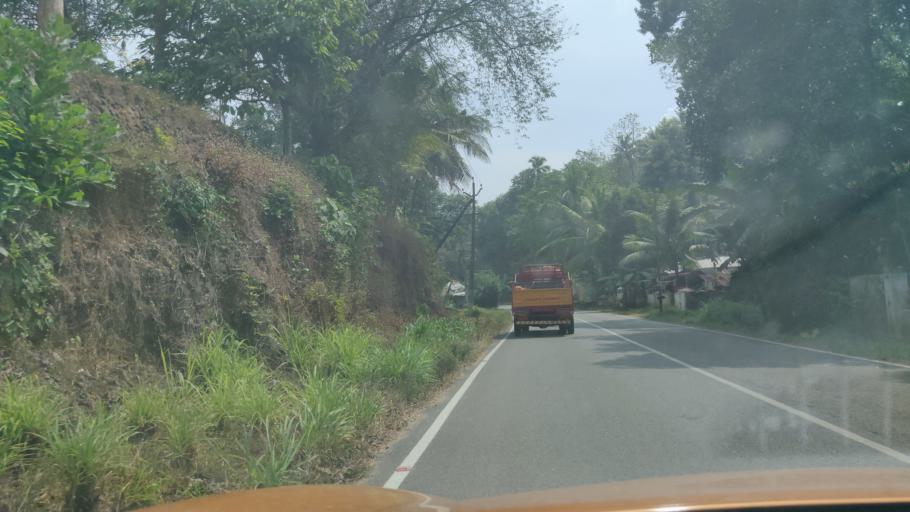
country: IN
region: Kerala
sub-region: Ernakulam
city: Muvattupuzha
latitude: 9.8858
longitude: 76.6548
